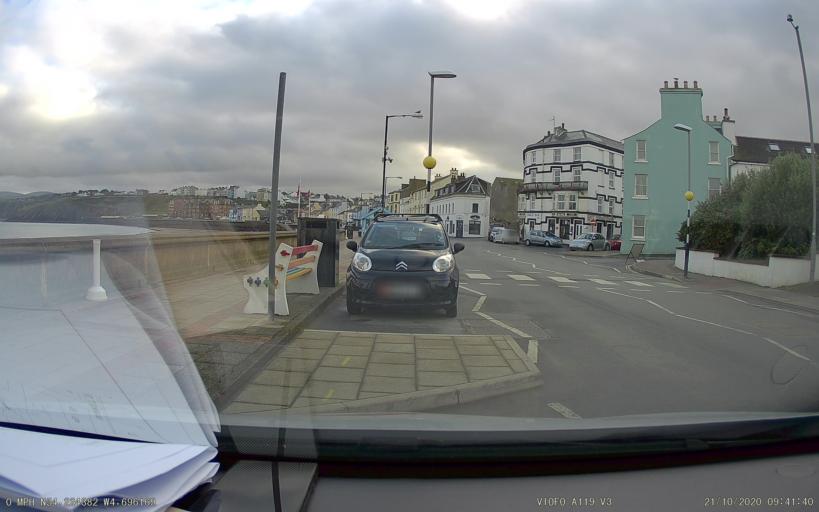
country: IM
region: Castletown
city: Castletown
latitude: 54.0000
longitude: -4.6962
